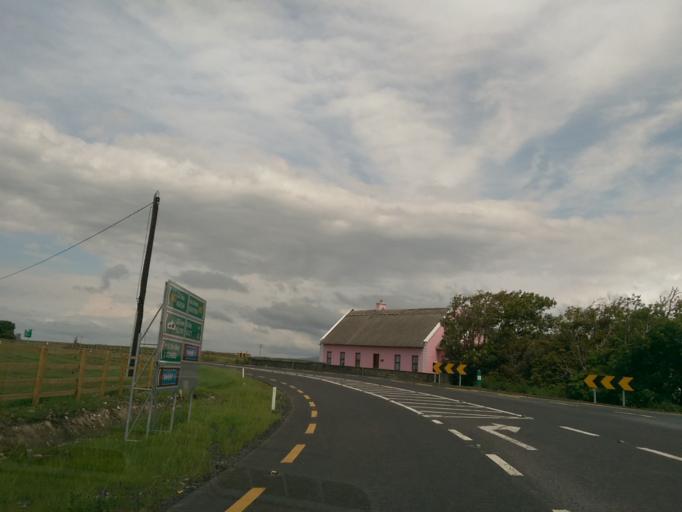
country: IE
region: Munster
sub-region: An Clar
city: Kilrush
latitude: 52.7374
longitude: -9.4831
